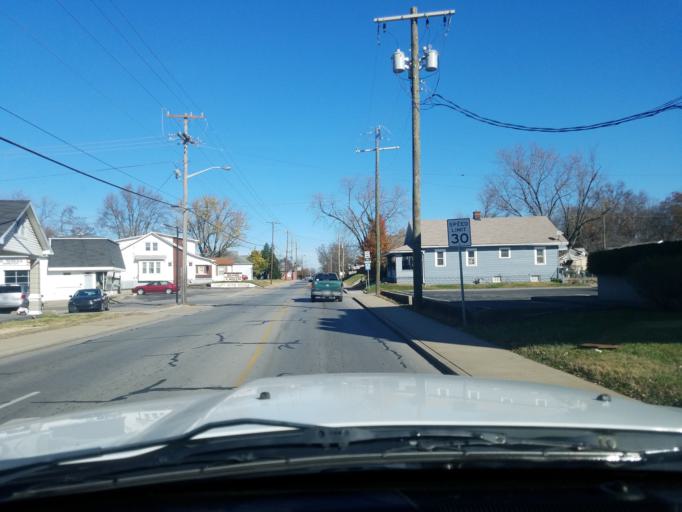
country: US
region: Indiana
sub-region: Floyd County
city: New Albany
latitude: 38.3072
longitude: -85.8100
